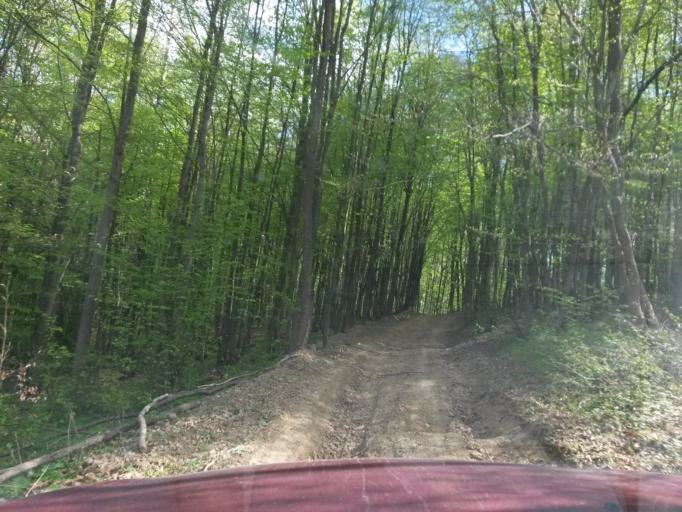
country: SK
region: Presovsky
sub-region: Okres Presov
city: Presov
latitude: 48.9529
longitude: 21.1333
